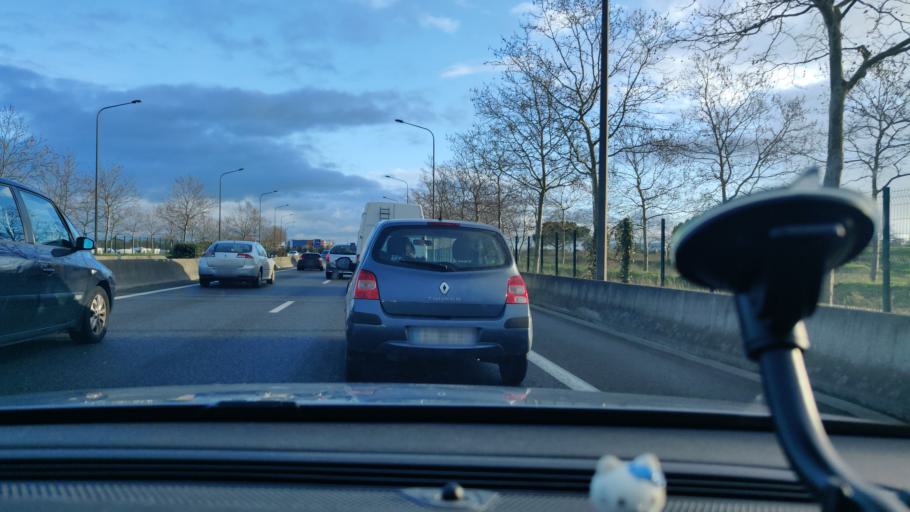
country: FR
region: Midi-Pyrenees
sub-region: Departement de la Haute-Garonne
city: Cugnaux
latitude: 43.5734
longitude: 1.3709
